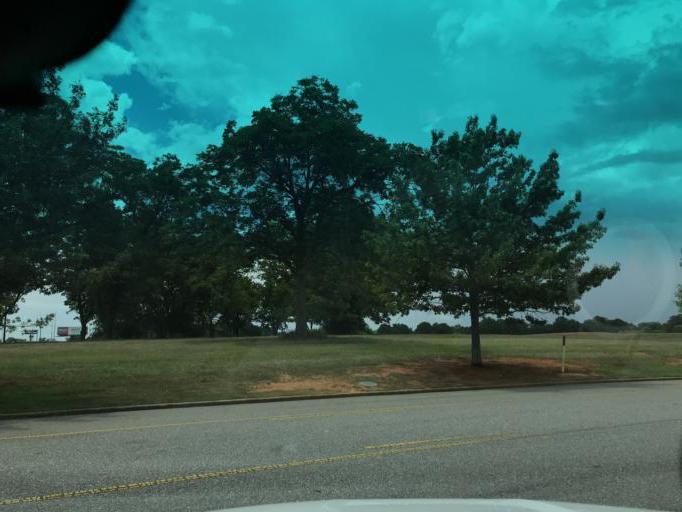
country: US
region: Alabama
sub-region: Montgomery County
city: Pike Road
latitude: 32.3694
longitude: -86.1322
